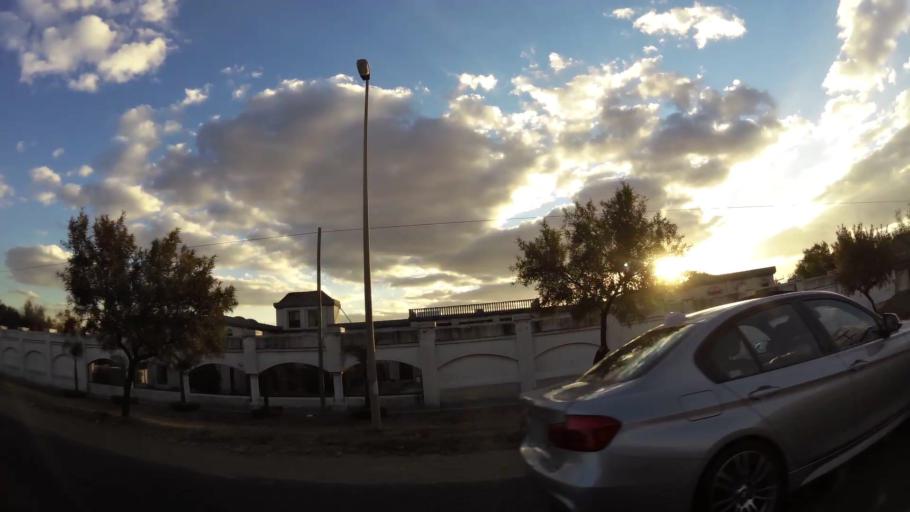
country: ZA
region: Gauteng
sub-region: City of Johannesburg Metropolitan Municipality
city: Midrand
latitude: -25.9743
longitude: 28.1532
